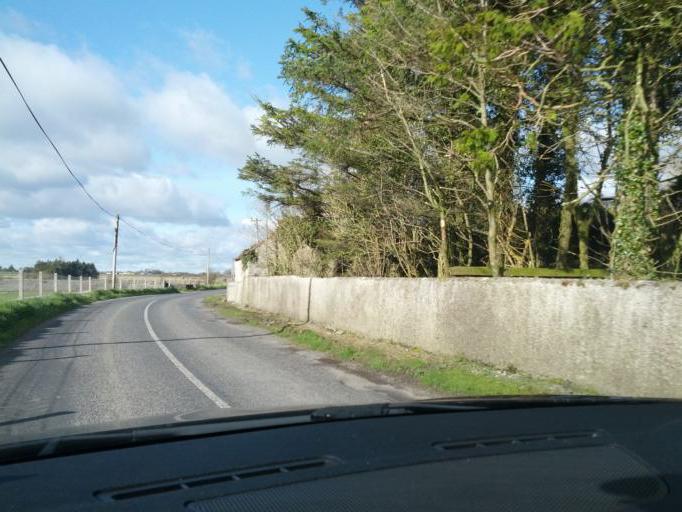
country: IE
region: Connaught
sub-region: County Galway
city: Athenry
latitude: 53.4278
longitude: -8.5736
